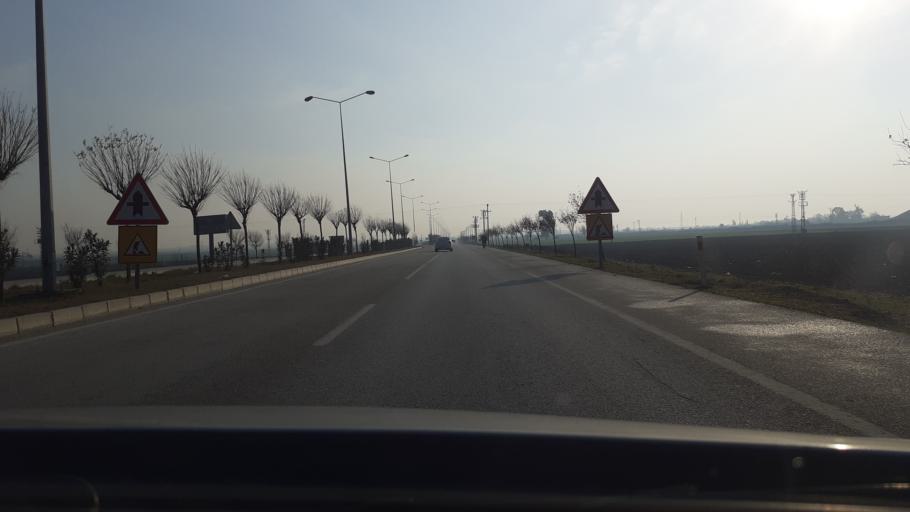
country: TR
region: Hatay
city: Serinyol
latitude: 36.3720
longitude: 36.2310
